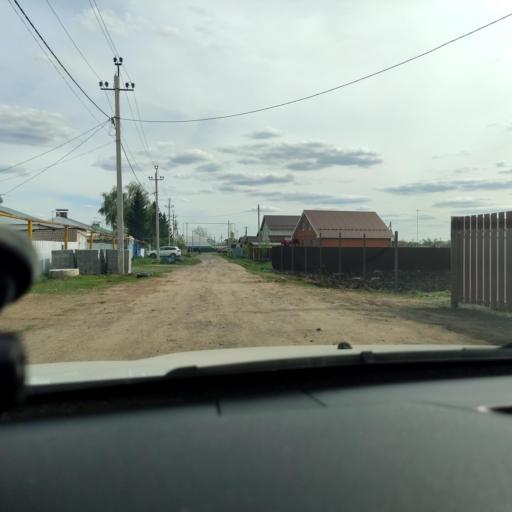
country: RU
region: Samara
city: Spiridonovka
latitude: 53.1602
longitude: 50.6470
